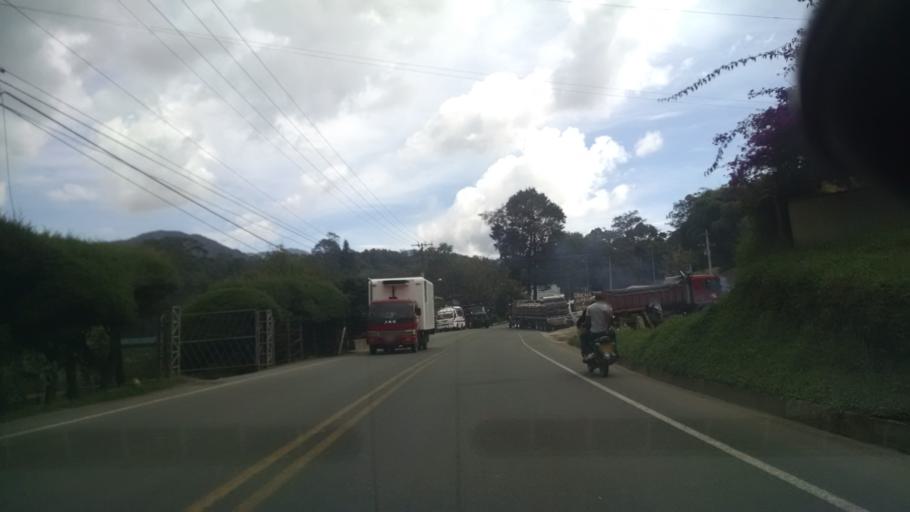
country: CO
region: Antioquia
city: Caldas
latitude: 6.0555
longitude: -75.6292
